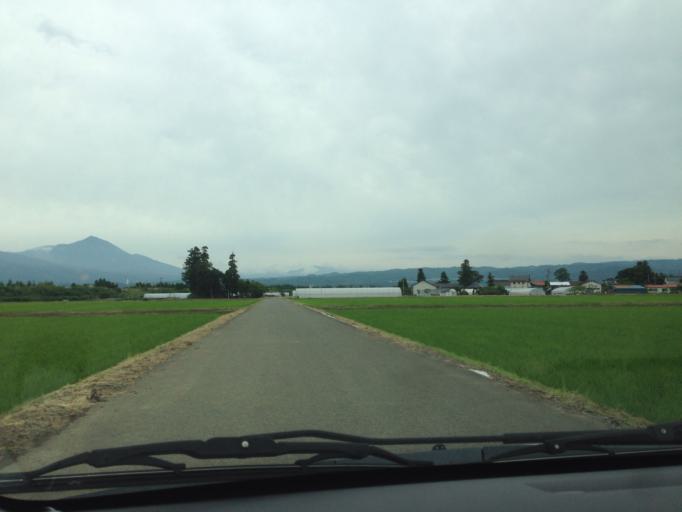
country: JP
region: Fukushima
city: Kitakata
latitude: 37.5336
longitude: 139.8934
